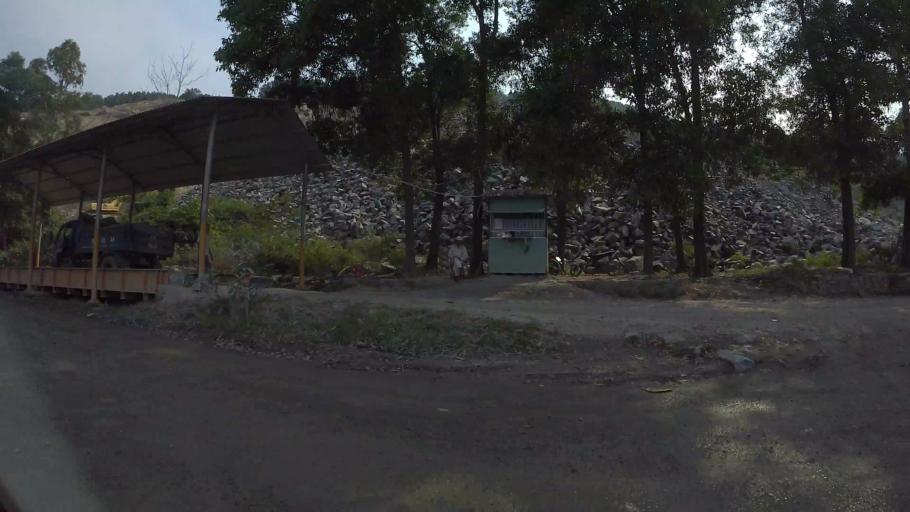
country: VN
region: Da Nang
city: Lien Chieu
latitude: 16.0382
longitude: 108.1535
